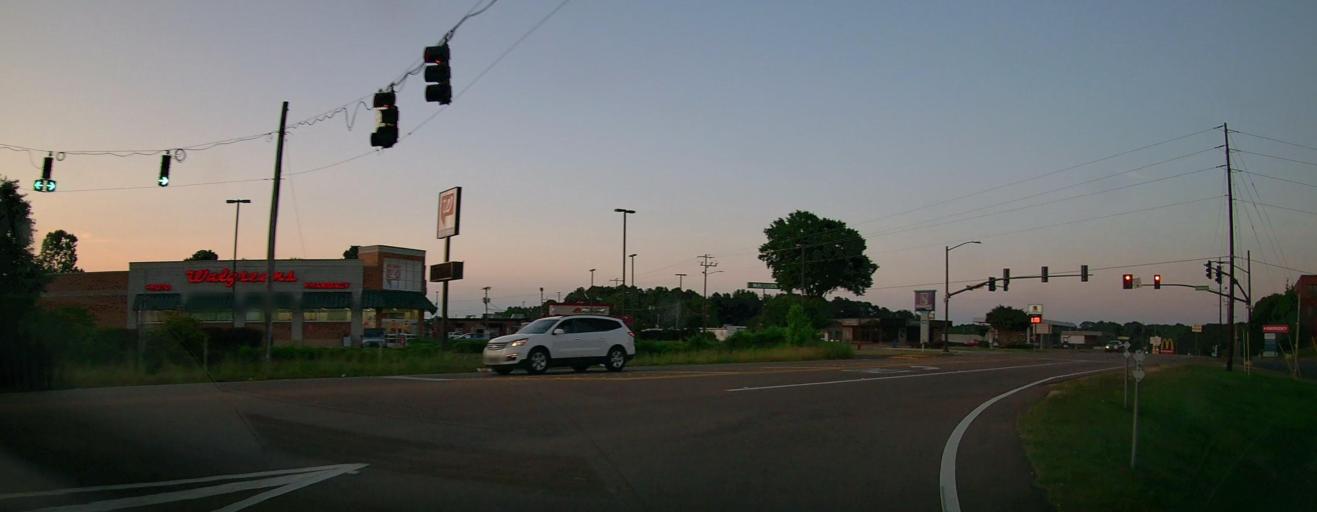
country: US
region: Mississippi
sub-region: Union County
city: New Albany
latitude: 34.4973
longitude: -89.0305
